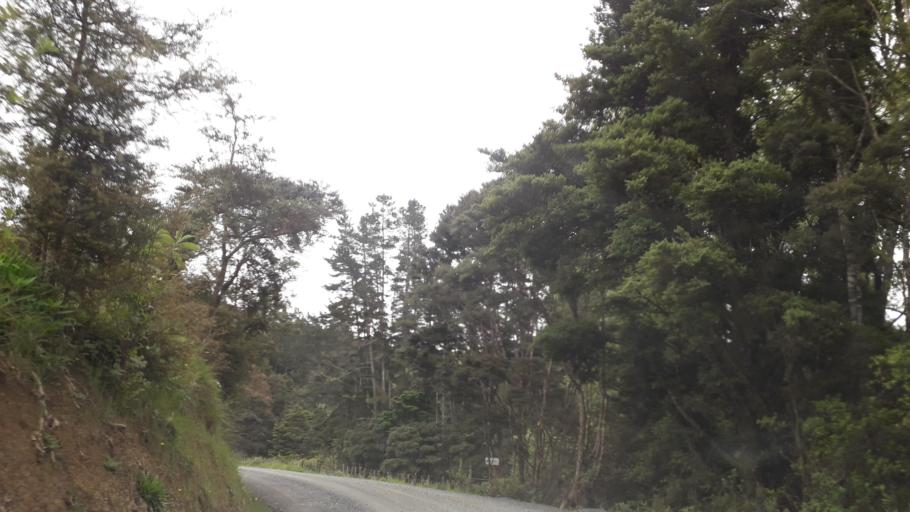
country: NZ
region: Northland
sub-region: Far North District
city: Taipa
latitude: -35.0670
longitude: 173.5516
